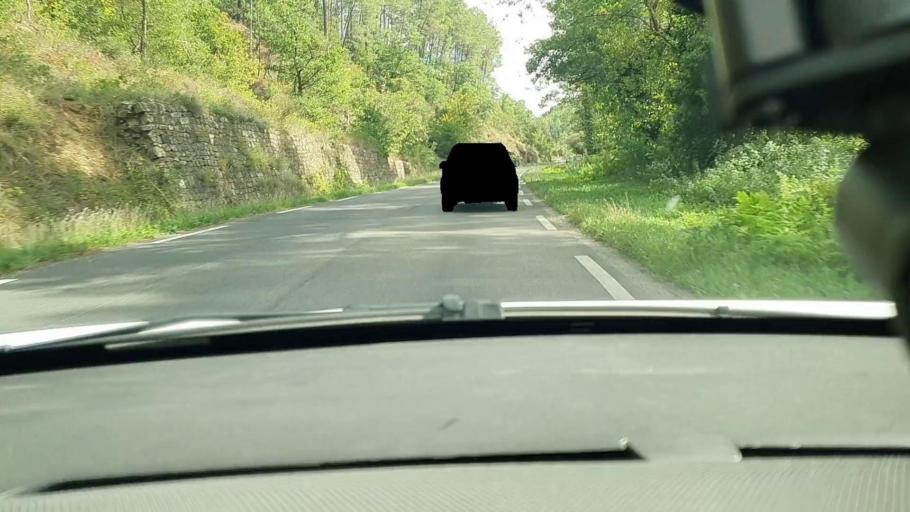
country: FR
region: Languedoc-Roussillon
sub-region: Departement du Gard
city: Saint-Florent-sur-Auzonnet
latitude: 44.2372
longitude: 4.1294
